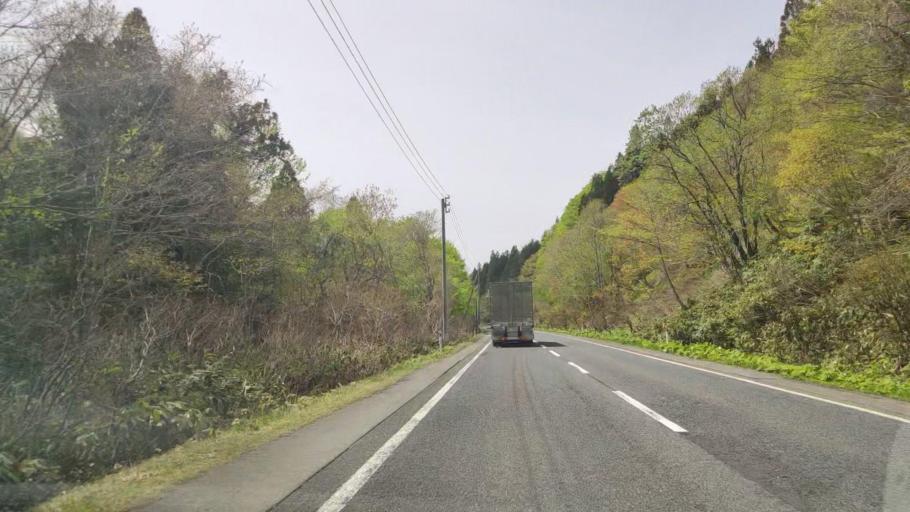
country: JP
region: Aomori
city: Aomori Shi
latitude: 40.7756
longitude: 141.0199
